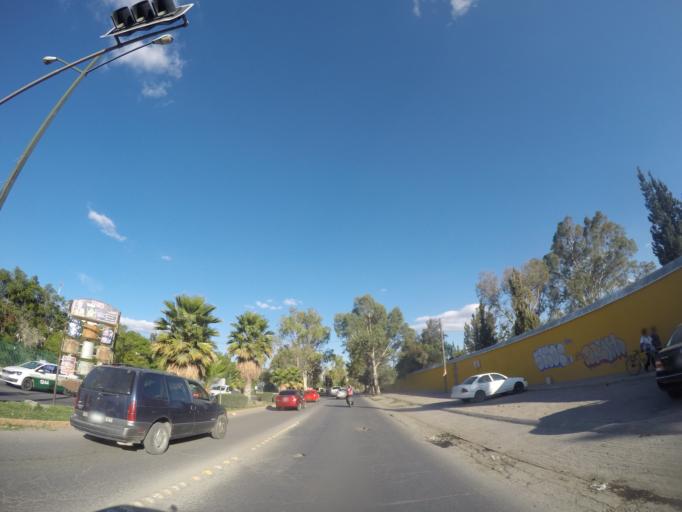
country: MX
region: San Luis Potosi
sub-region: San Luis Potosi
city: San Luis Potosi
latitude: 22.1813
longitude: -100.9981
